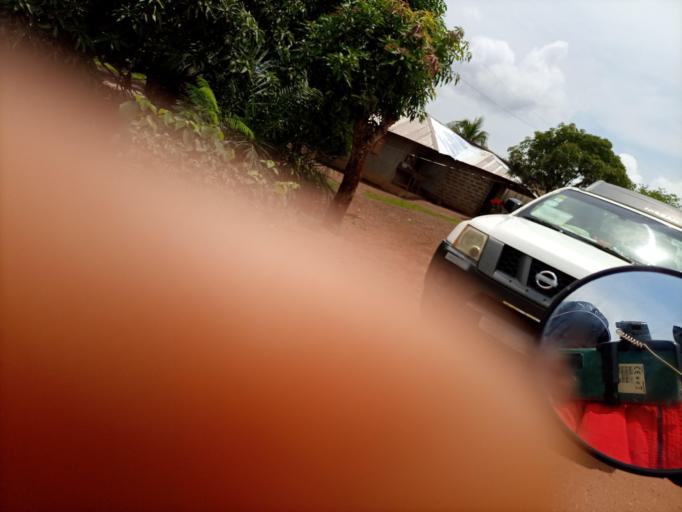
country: SL
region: Southern Province
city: Bo
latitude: 7.9725
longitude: -11.7213
